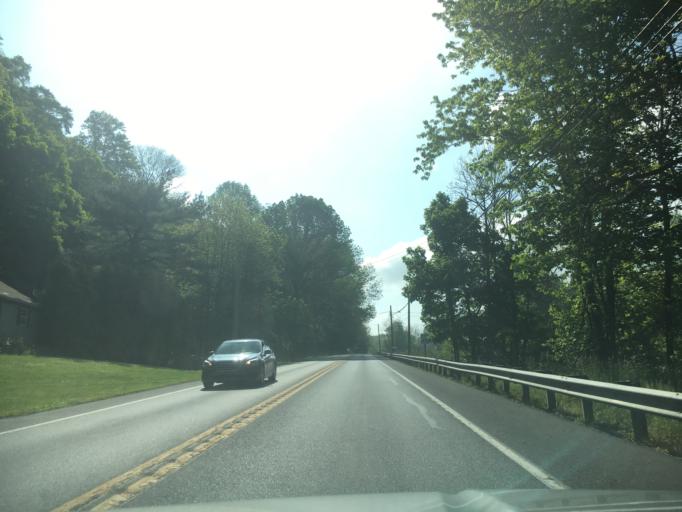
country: US
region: Pennsylvania
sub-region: Berks County
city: Oley
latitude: 40.3734
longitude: -75.7177
